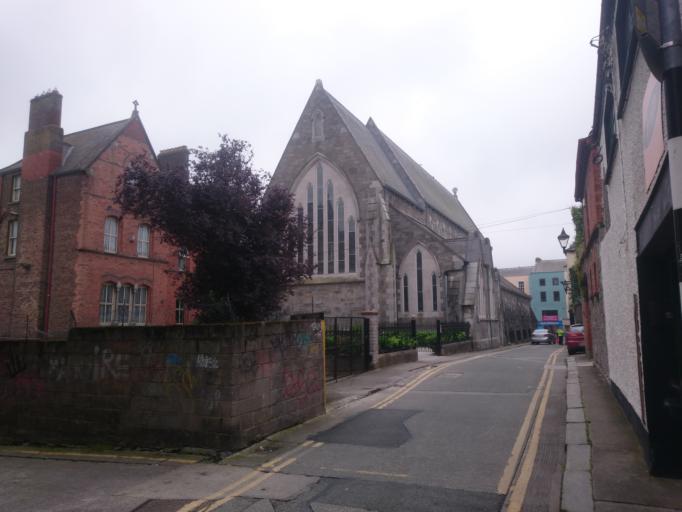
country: IE
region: Leinster
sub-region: Lu
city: Drogheda
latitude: 53.7149
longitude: -6.3489
